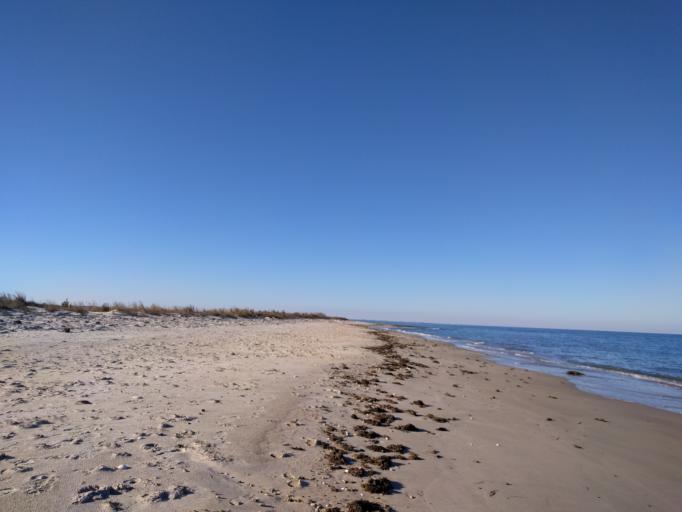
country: US
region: Virginia
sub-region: City of Poquoson
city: Poquoson
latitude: 37.0982
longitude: -76.2775
